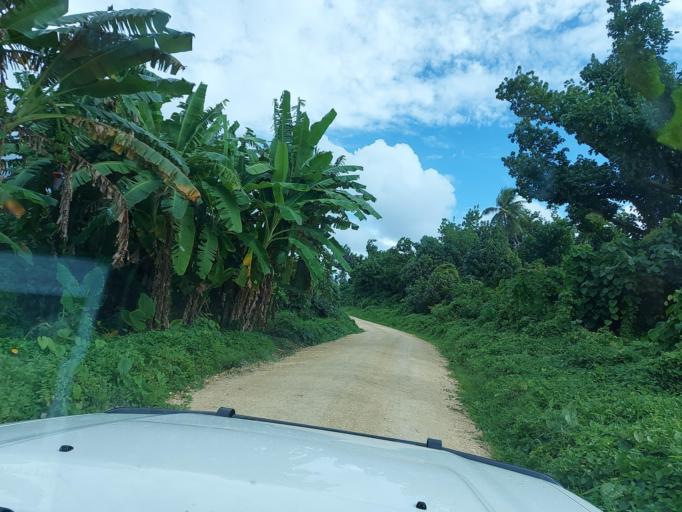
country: VU
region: Penama
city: Saratamata
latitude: -15.9610
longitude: 168.1935
